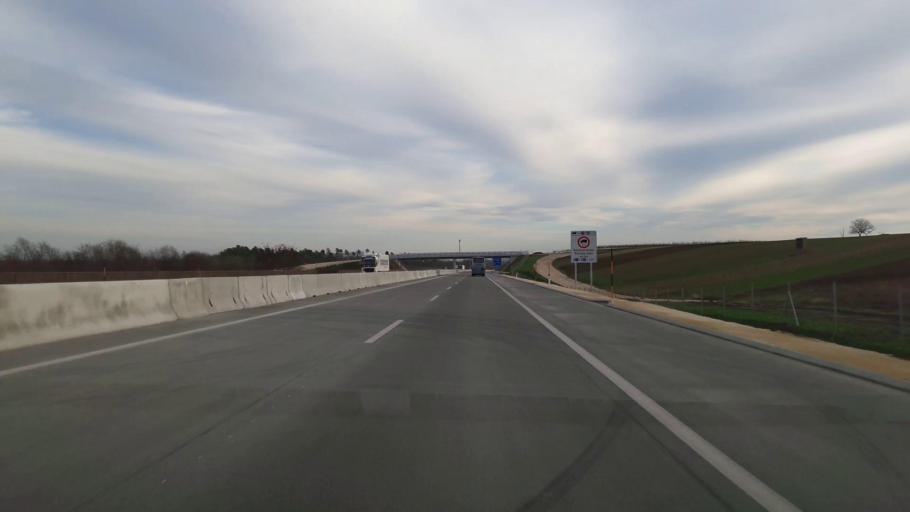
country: AT
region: Lower Austria
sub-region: Politischer Bezirk Mistelbach
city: Herrnbaumgarten
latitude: 48.6658
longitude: 16.6812
